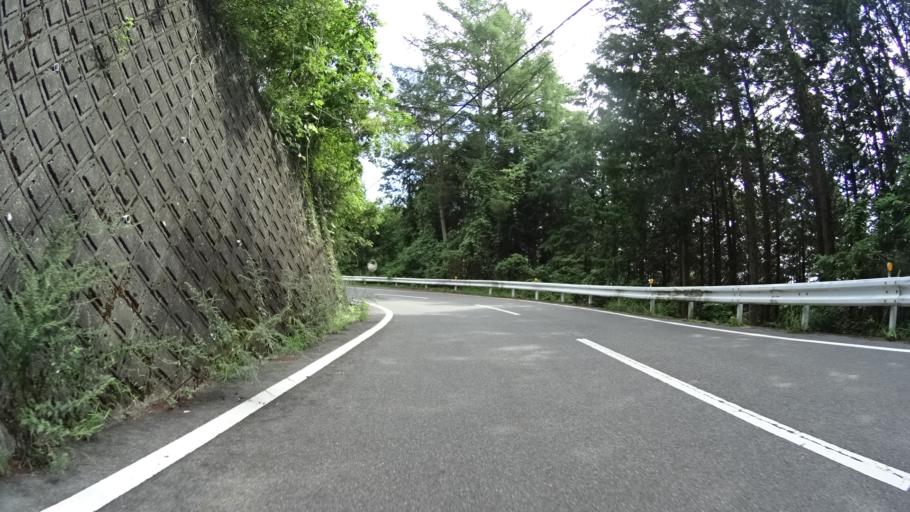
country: JP
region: Yamanashi
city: Kofu-shi
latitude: 35.7676
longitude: 138.5508
